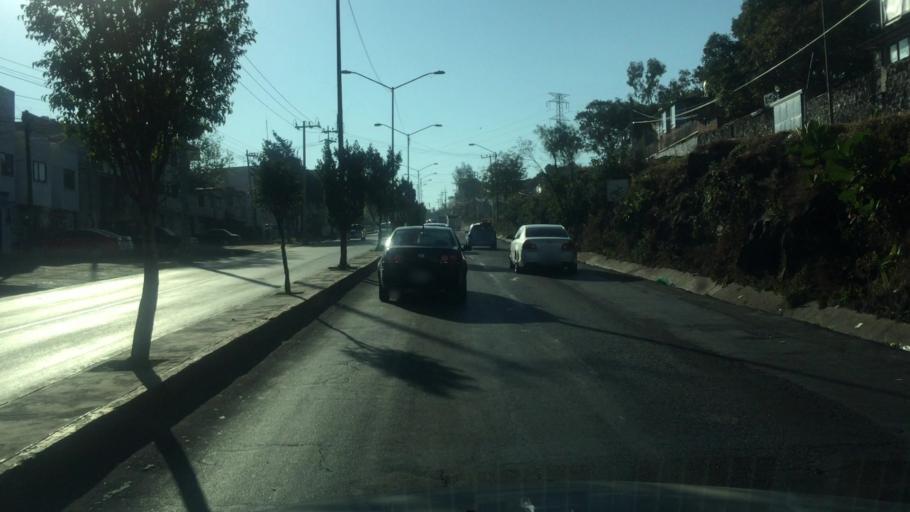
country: MX
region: Mexico City
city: Tlalpan
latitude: 19.2765
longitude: -99.2089
